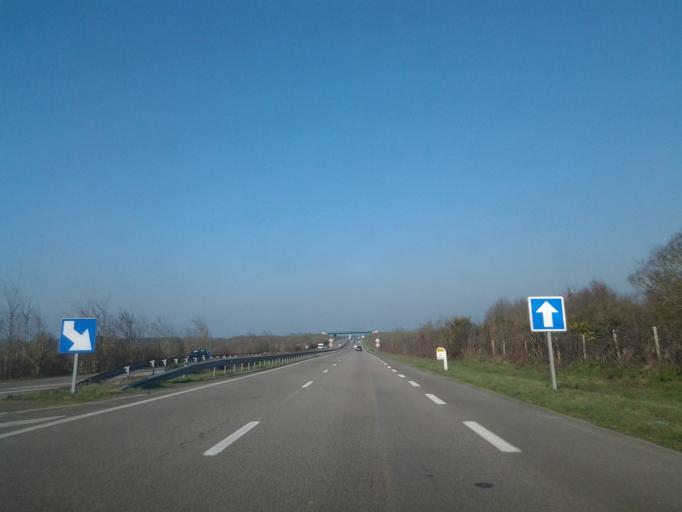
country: FR
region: Pays de la Loire
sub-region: Departement de la Vendee
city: Mache
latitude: 46.7908
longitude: -1.7069
